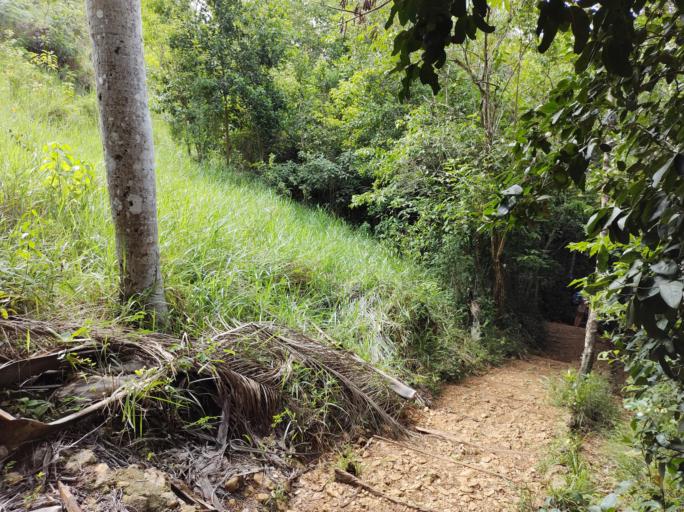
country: DO
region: Samana
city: Las Terrenas
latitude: 19.2715
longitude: -69.4443
